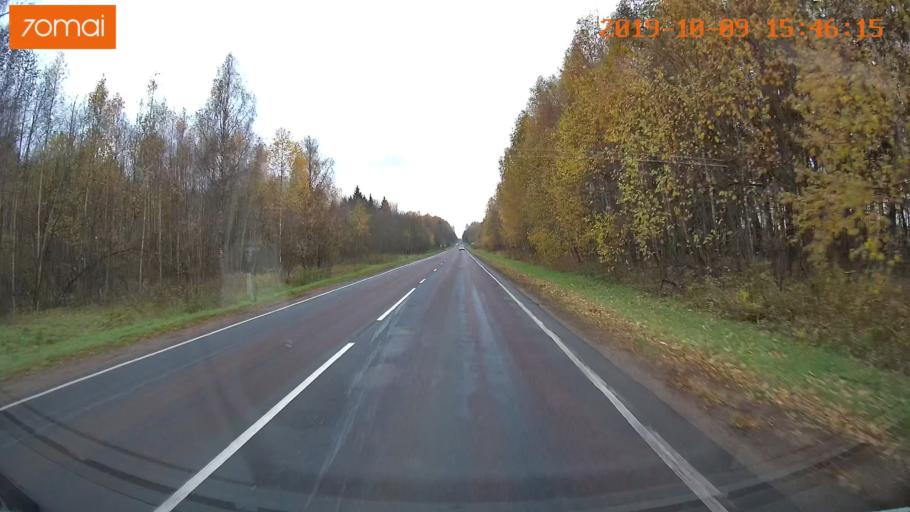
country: RU
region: Kostroma
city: Oktyabr'skiy
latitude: 57.8265
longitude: 41.0479
